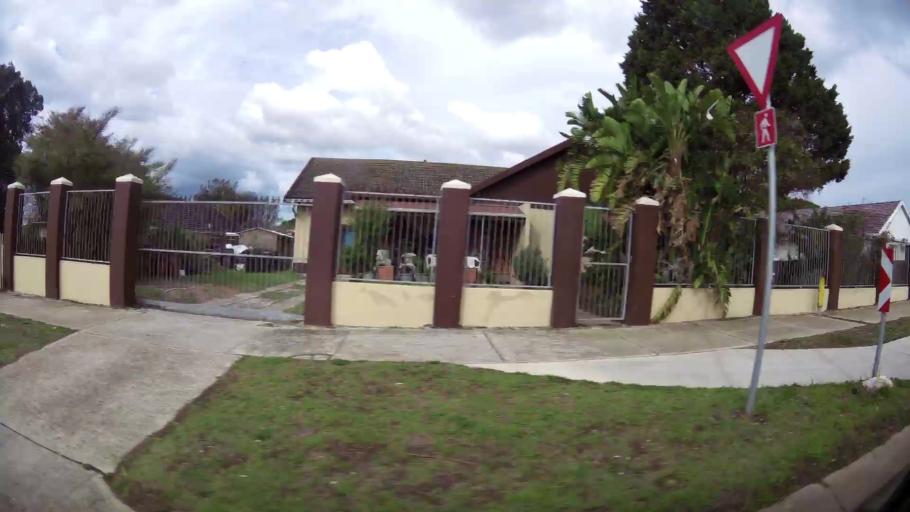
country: ZA
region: Eastern Cape
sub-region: Nelson Mandela Bay Metropolitan Municipality
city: Port Elizabeth
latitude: -33.9345
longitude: 25.5126
